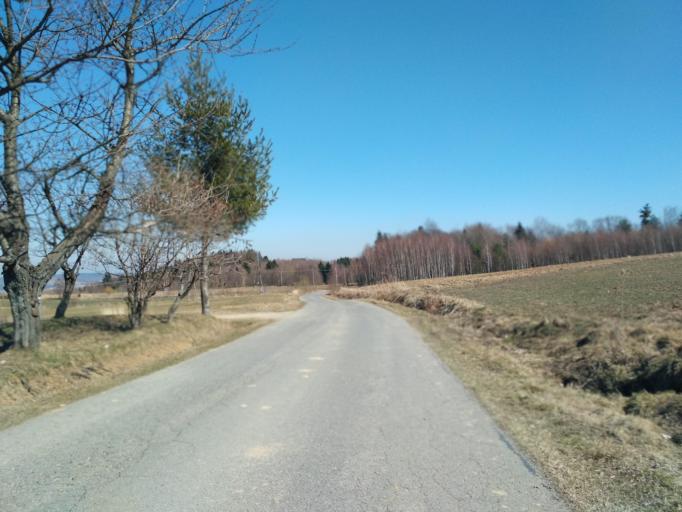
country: PL
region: Subcarpathian Voivodeship
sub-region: Powiat ropczycko-sedziszowski
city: Niedzwiada
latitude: 49.9506
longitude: 21.5008
